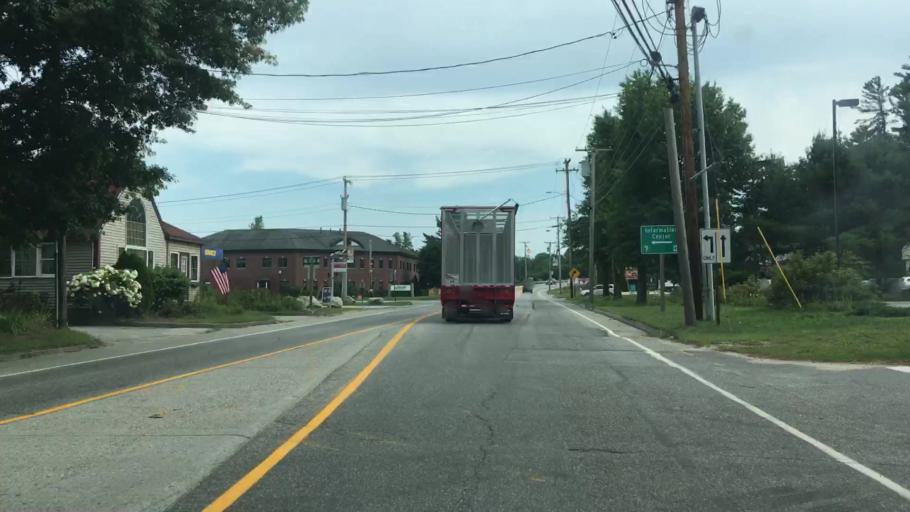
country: US
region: Maine
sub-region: Oxford County
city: Bethel
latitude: 44.4132
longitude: -70.7959
